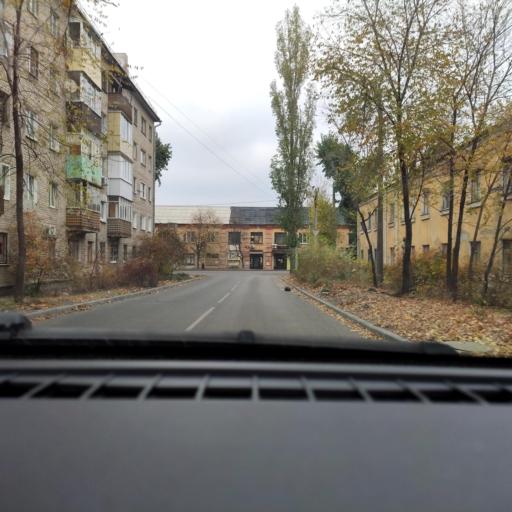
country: RU
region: Voronezj
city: Maslovka
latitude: 51.6195
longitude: 39.2472
